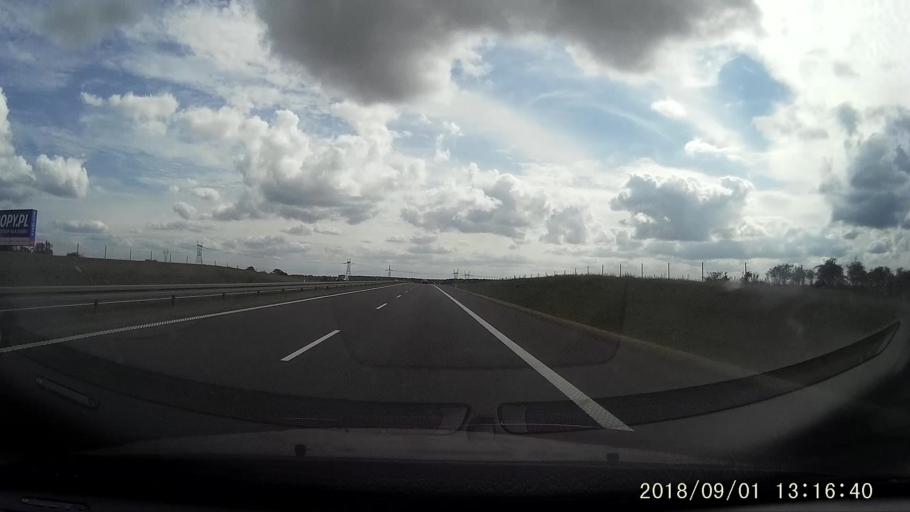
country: PL
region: West Pomeranian Voivodeship
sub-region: Powiat pyrzycki
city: Bielice
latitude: 53.2349
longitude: 14.6395
